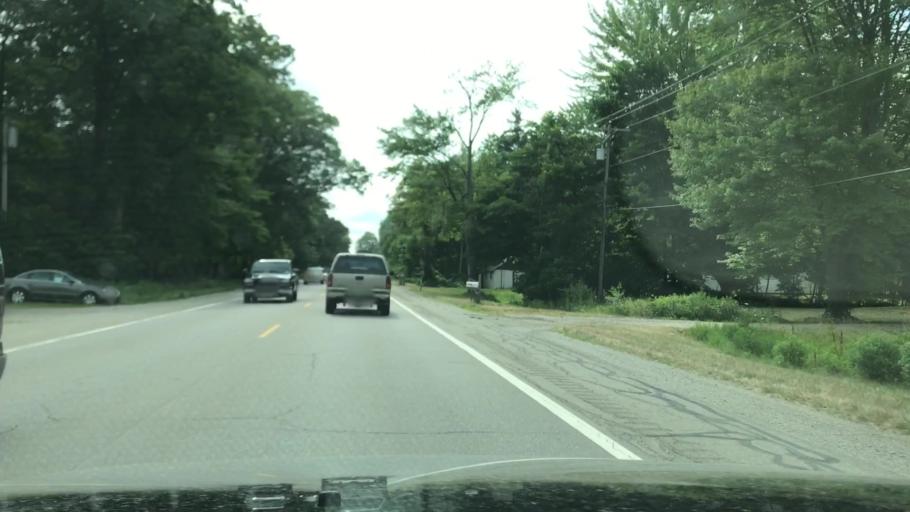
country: US
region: Michigan
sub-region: Muskegon County
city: Fruitport
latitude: 43.0739
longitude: -86.1282
